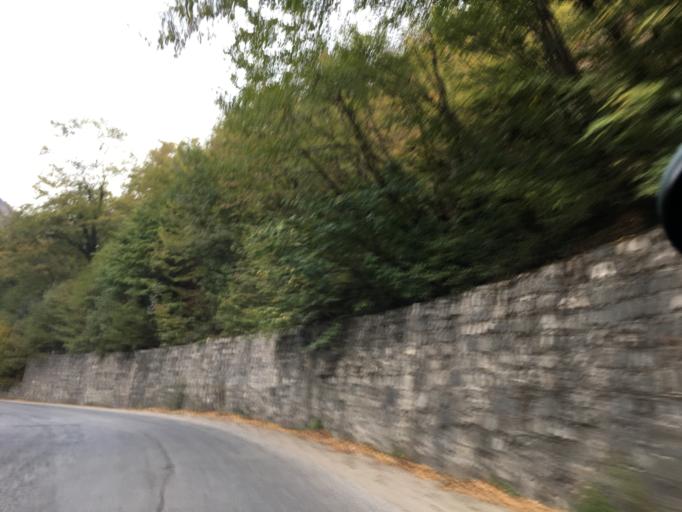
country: BG
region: Pazardzhik
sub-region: Obshtina Belovo
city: Belovo
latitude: 42.1664
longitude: 23.9759
